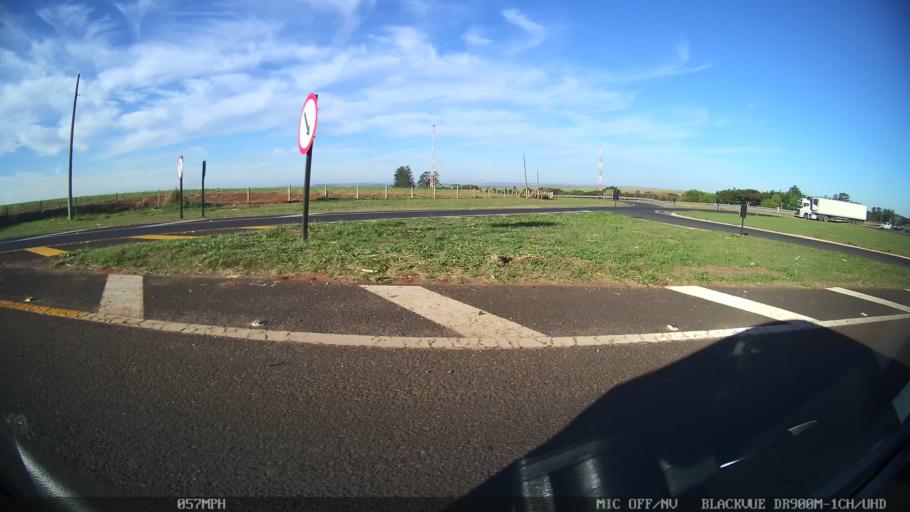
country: BR
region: Sao Paulo
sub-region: Americo Brasiliense
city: Americo Brasiliense
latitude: -21.7745
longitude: -48.1020
